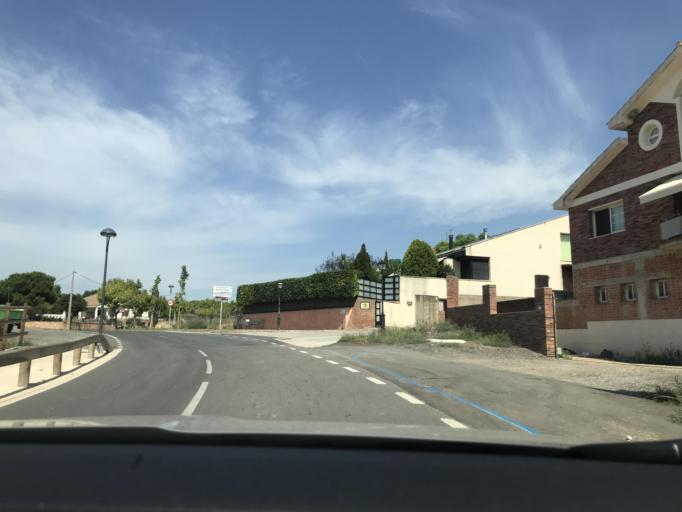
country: ES
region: Catalonia
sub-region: Provincia de Tarragona
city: Salomo
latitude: 41.2261
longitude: 1.3755
